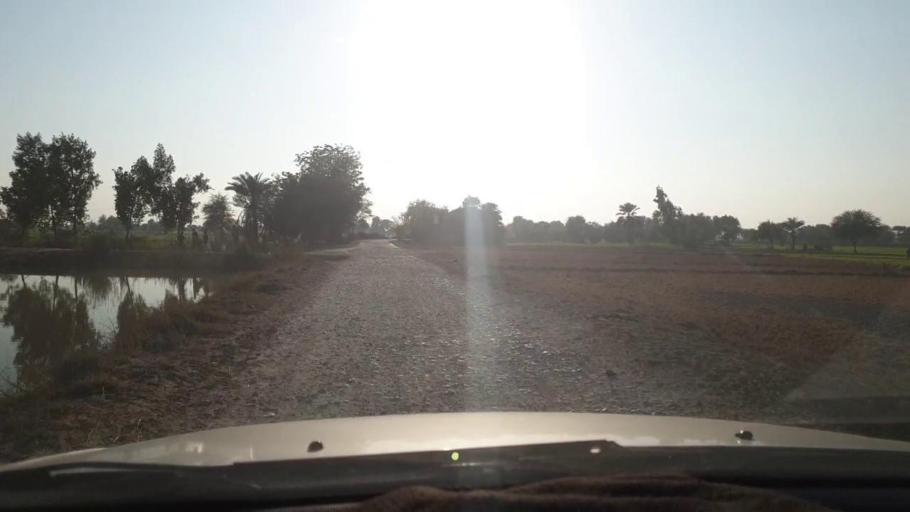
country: PK
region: Sindh
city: Mirpur Mathelo
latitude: 27.9985
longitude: 69.5236
